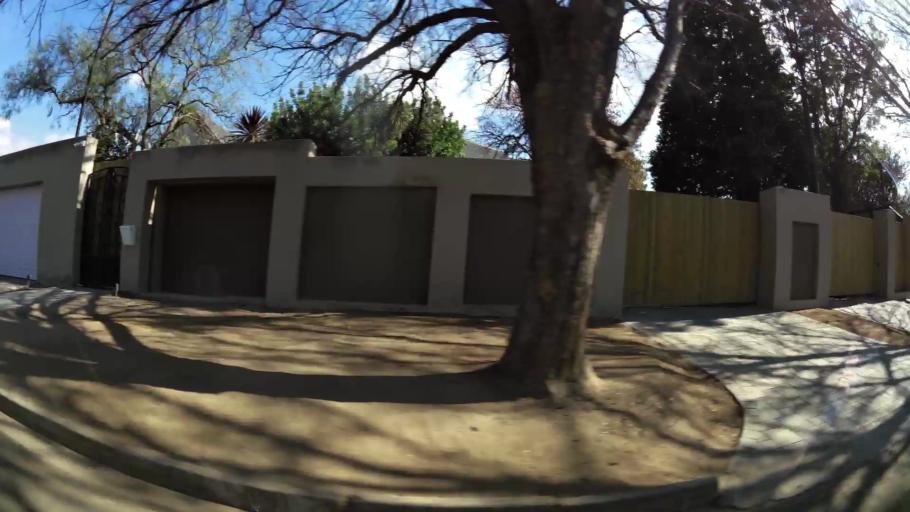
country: ZA
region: Gauteng
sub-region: Ekurhuleni Metropolitan Municipality
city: Benoni
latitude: -26.1425
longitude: 28.3476
